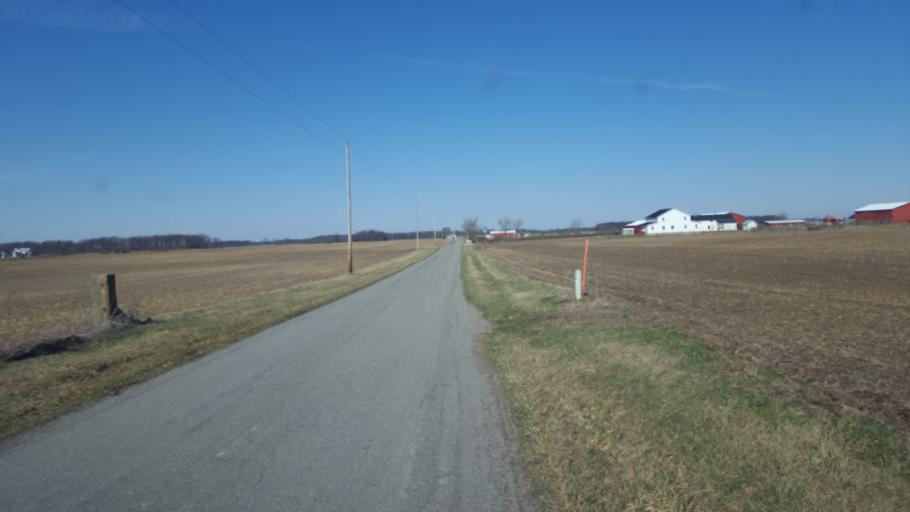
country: US
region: Ohio
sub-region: Union County
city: Richwood
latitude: 40.5330
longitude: -83.4555
